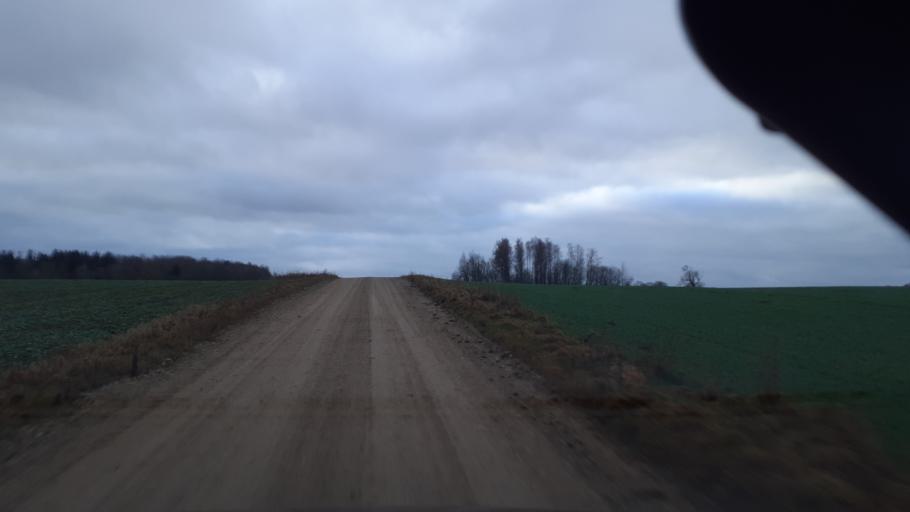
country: LV
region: Kuldigas Rajons
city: Kuldiga
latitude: 56.8668
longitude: 21.7713
